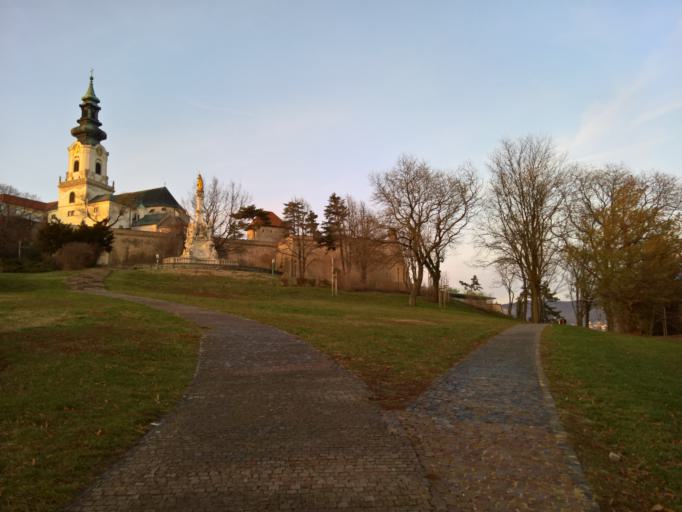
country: SK
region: Nitriansky
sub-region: Okres Nitra
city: Nitra
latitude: 48.3172
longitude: 18.0883
